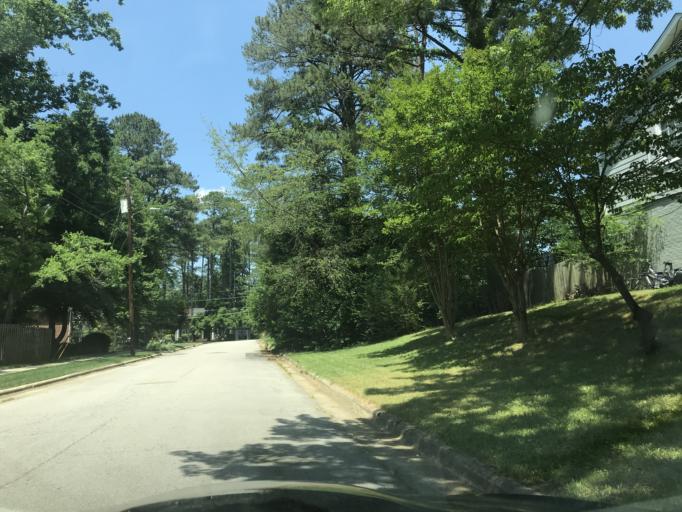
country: US
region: North Carolina
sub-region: Wake County
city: West Raleigh
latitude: 35.8469
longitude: -78.6164
